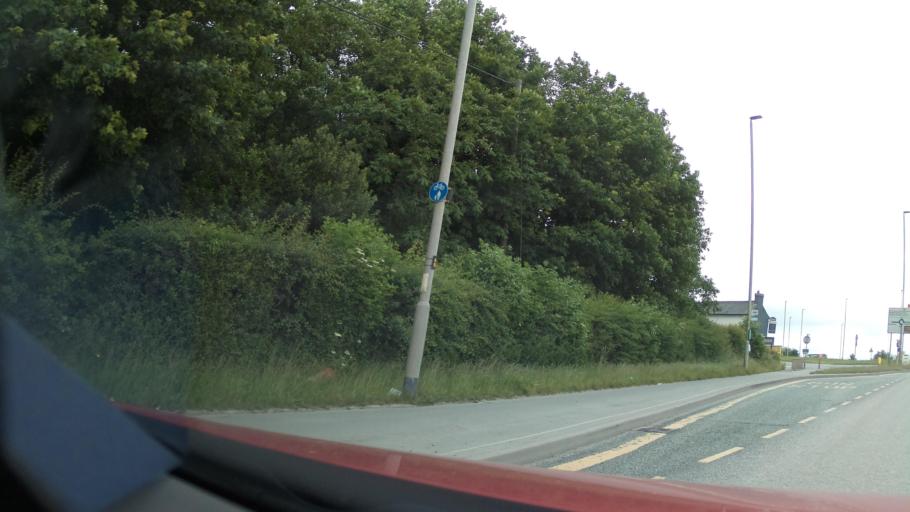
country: GB
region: England
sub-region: Leicestershire
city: Coalville
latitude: 52.7104
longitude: -1.3414
